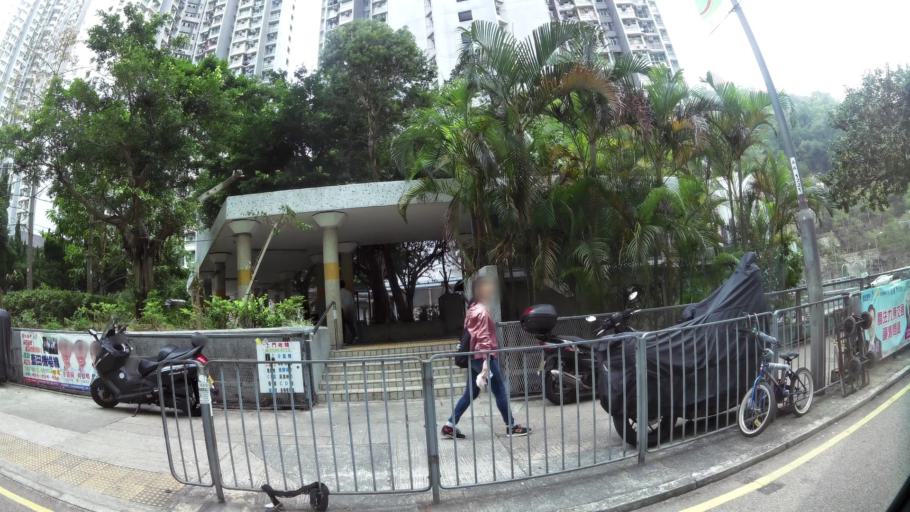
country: HK
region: Kowloon City
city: Kowloon
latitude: 22.3023
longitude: 114.2407
